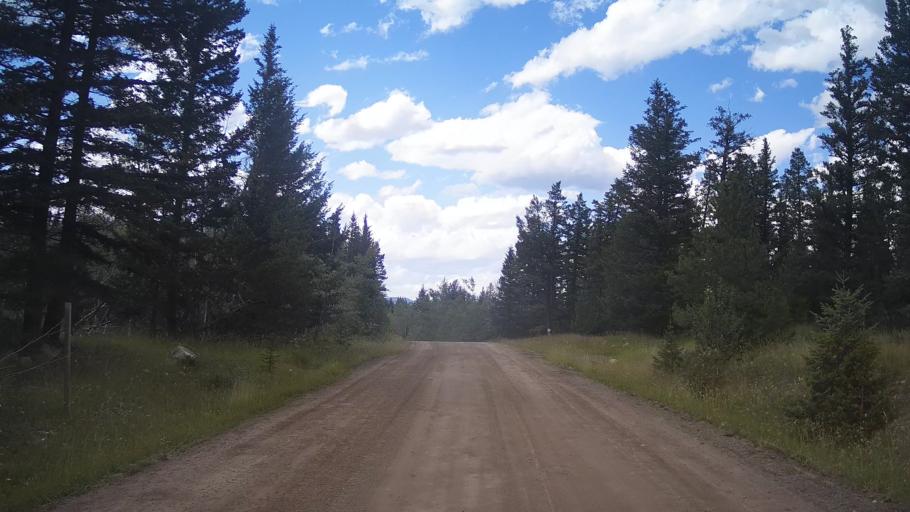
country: CA
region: British Columbia
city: Lillooet
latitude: 51.3348
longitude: -121.9018
